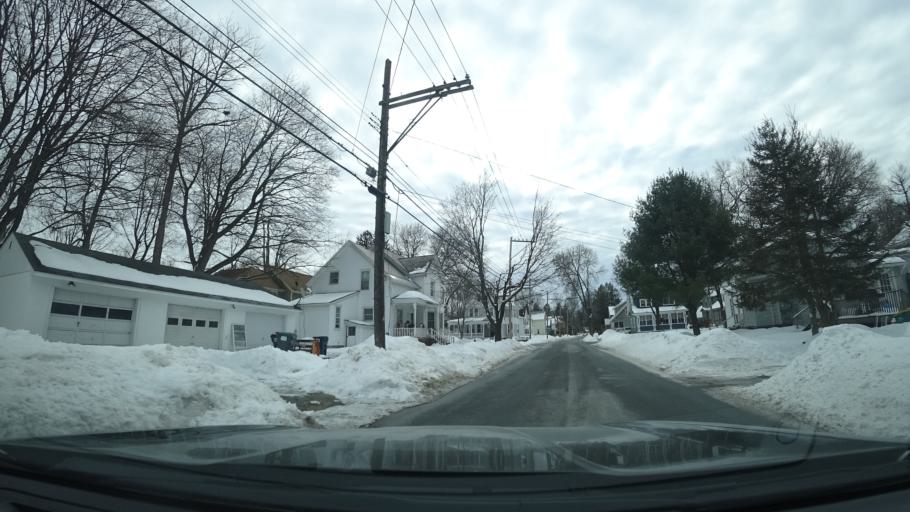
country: US
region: New York
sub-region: Warren County
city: Glens Falls
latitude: 43.3131
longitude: -73.6561
